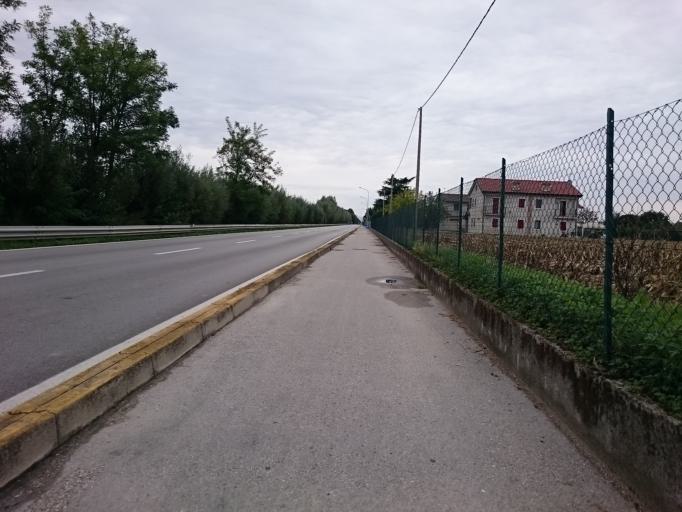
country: IT
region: Veneto
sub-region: Provincia di Vicenza
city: Quinto Vicentino
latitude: 45.5691
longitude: 11.6462
